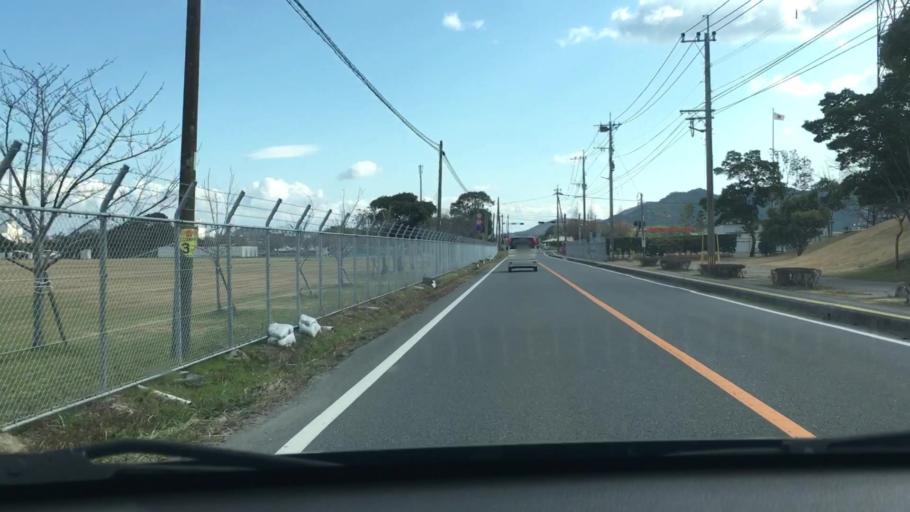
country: JP
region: Oita
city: Saiki
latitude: 32.9697
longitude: 131.9131
